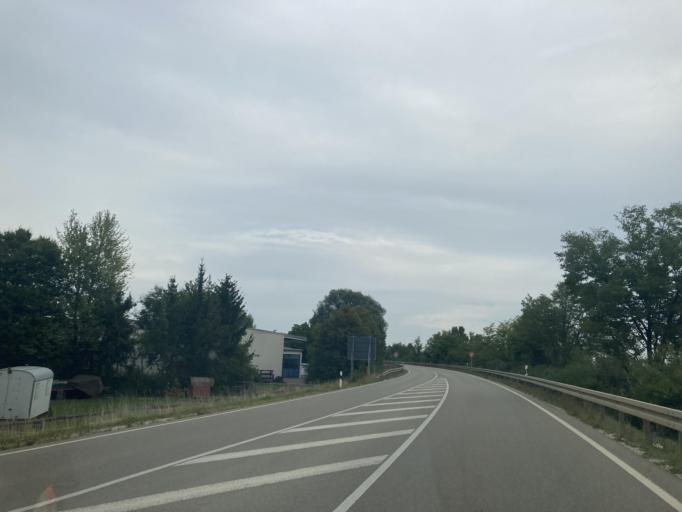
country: DE
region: Bavaria
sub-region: Swabia
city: Deiningen
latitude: 48.8724
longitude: 10.5410
